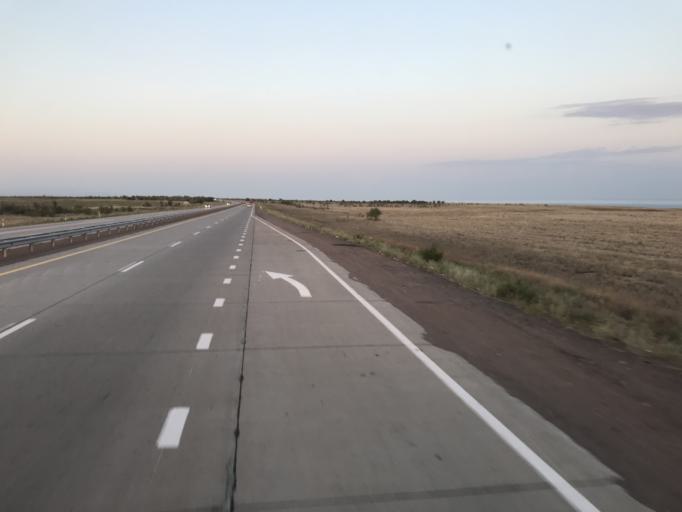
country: KZ
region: Almaty Oblysy
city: Kapshagay
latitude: 43.9236
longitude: 77.1686
